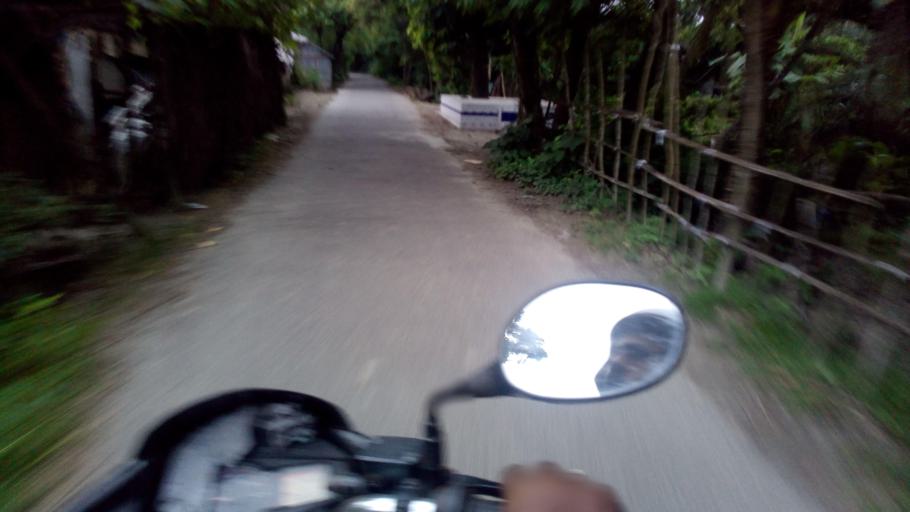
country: BD
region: Khulna
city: Phultala
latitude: 22.7548
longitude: 89.4077
